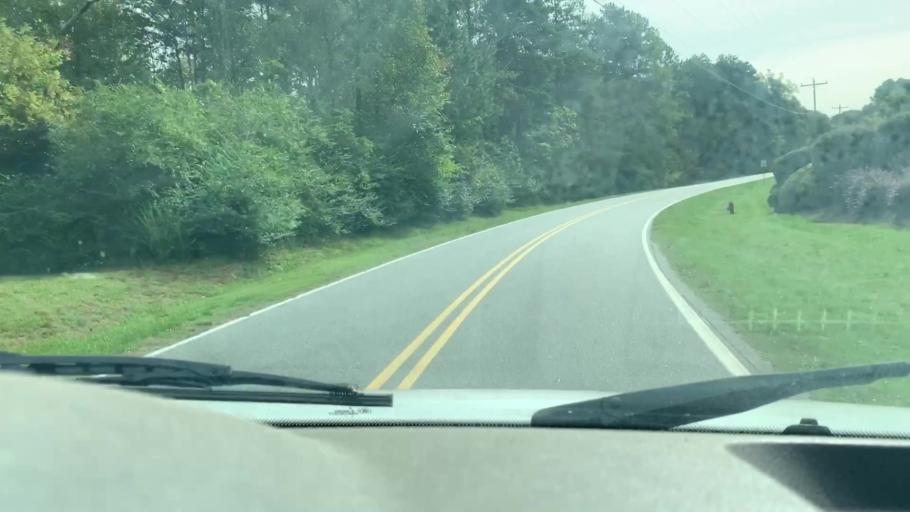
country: US
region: North Carolina
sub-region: Catawba County
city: Lake Norman of Catawba
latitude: 35.5728
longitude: -80.9367
